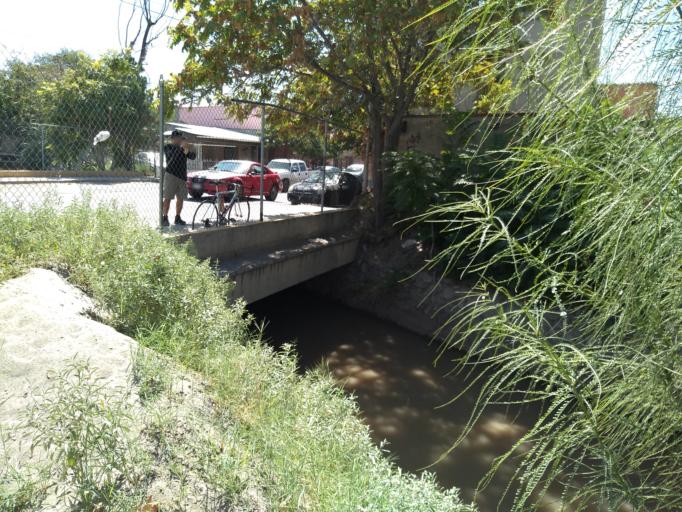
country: MX
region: Chihuahua
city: Ciudad Juarez
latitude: 31.7444
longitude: -106.4896
